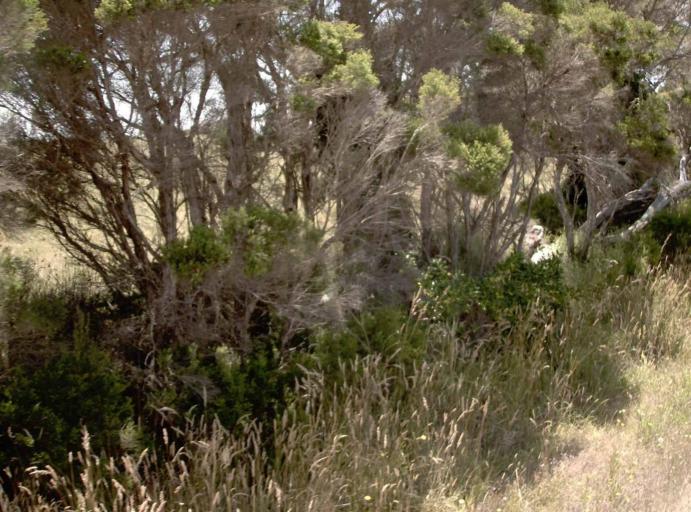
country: AU
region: Victoria
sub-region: Bass Coast
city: North Wonthaggi
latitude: -38.6685
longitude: 145.9775
